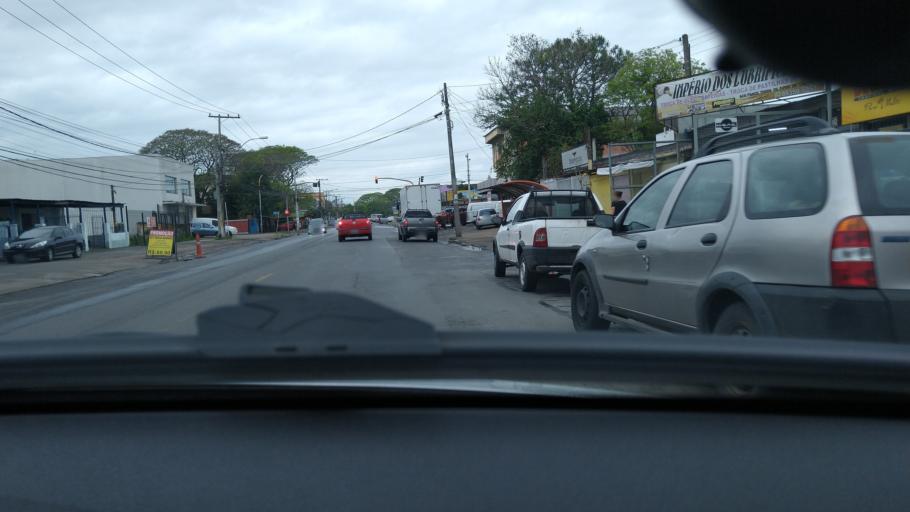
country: BR
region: Rio Grande do Sul
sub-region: Canoas
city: Canoas
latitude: -29.9027
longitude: -51.1919
